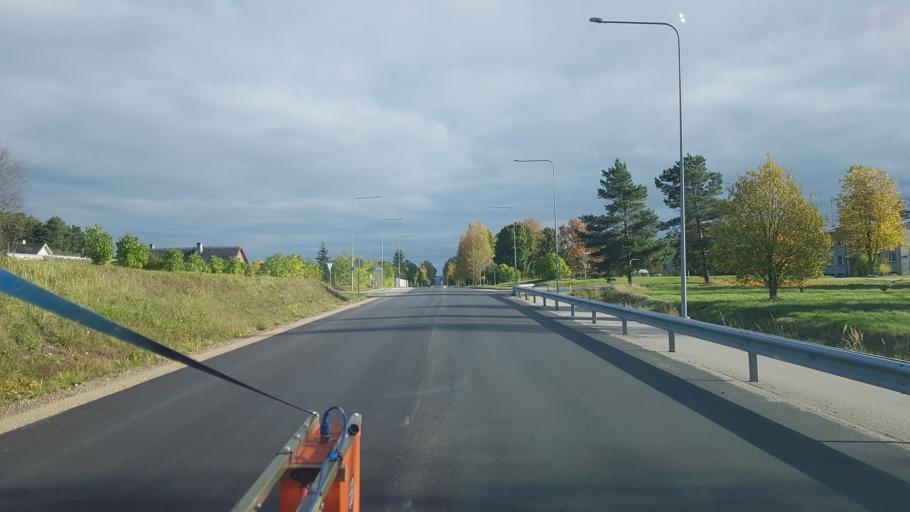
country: EE
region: Vorumaa
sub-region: Voru linn
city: Voru
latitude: 57.8161
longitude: 27.0325
